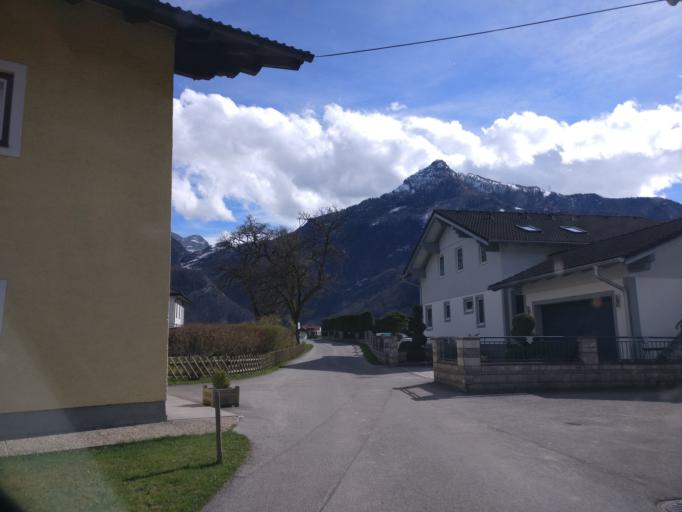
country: AT
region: Salzburg
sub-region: Politischer Bezirk Hallein
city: Golling an der Salzach
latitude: 47.5965
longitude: 13.1559
